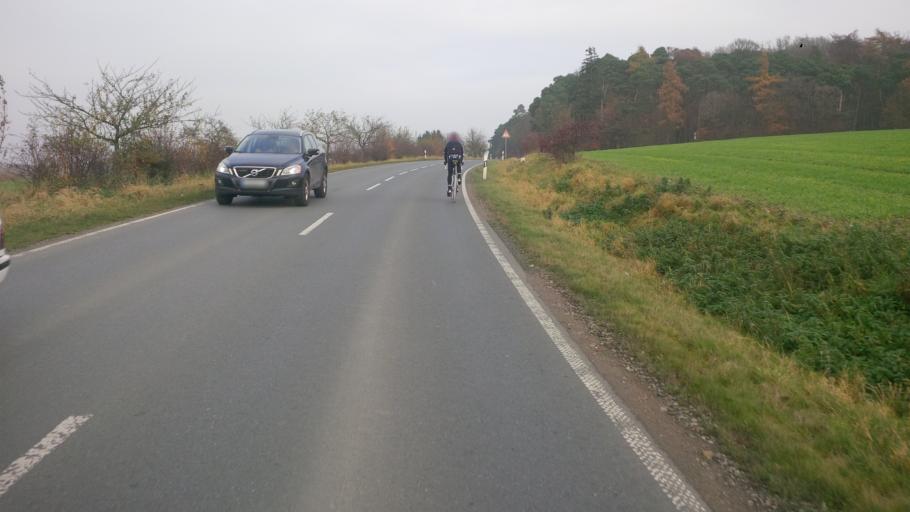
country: DE
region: Hesse
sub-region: Regierungsbezirk Darmstadt
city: Wehrheim
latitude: 50.3117
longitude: 8.5772
